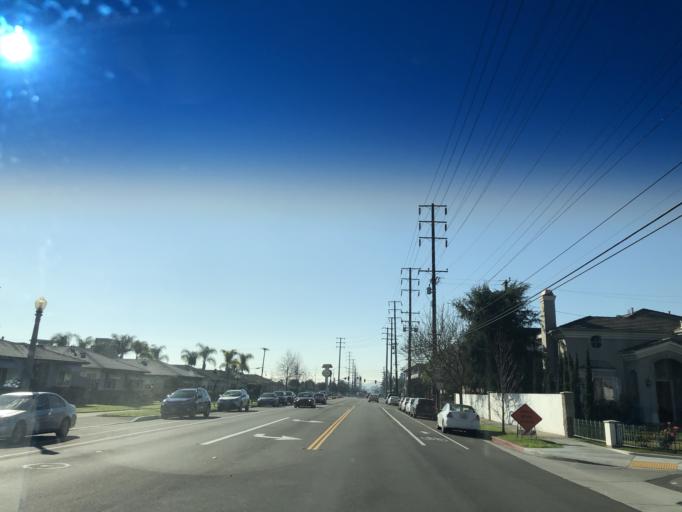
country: US
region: California
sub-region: Los Angeles County
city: East San Gabriel
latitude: 34.0818
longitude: -118.0996
